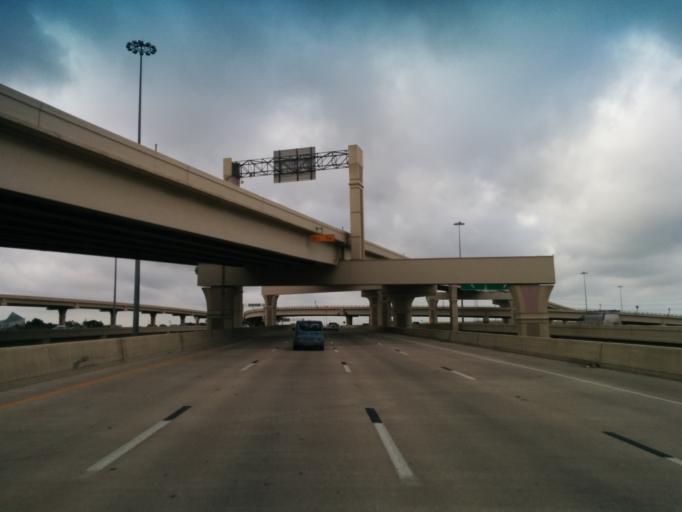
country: US
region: Texas
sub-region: Bexar County
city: Balcones Heights
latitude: 29.5023
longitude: -98.5494
